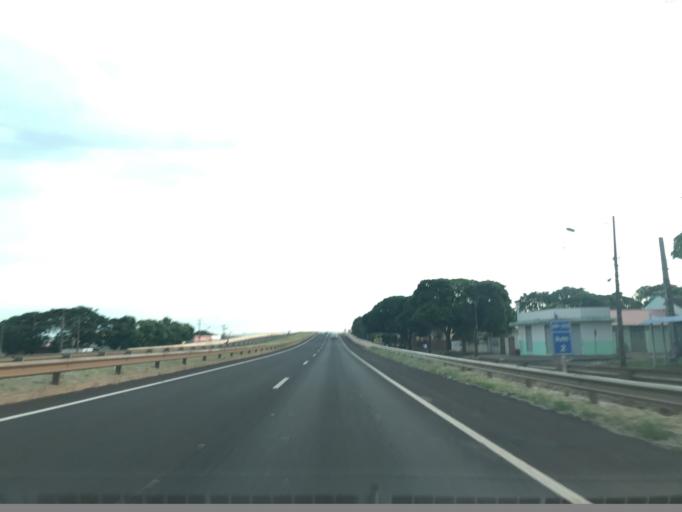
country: BR
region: Parana
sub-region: Maringa
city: Maringa
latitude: -23.3966
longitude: -51.9750
